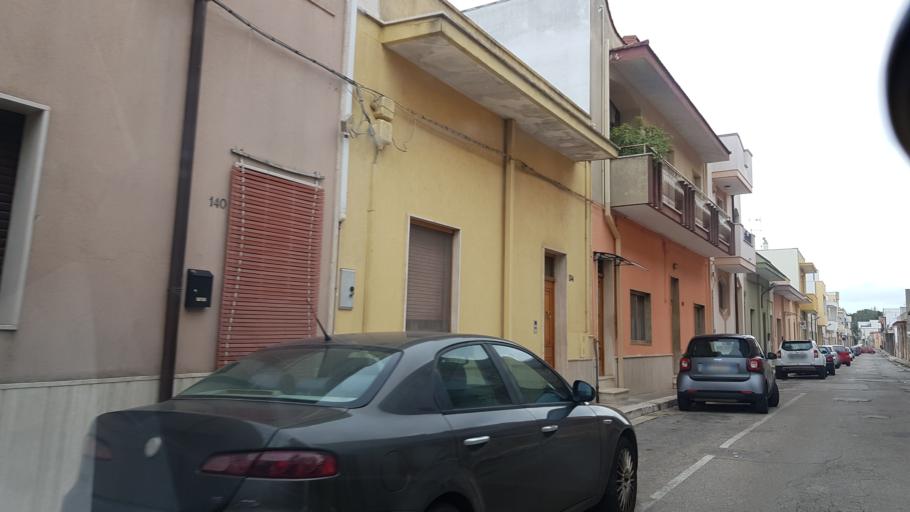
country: IT
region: Apulia
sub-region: Provincia di Brindisi
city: Mesagne
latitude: 40.5639
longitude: 17.8068
